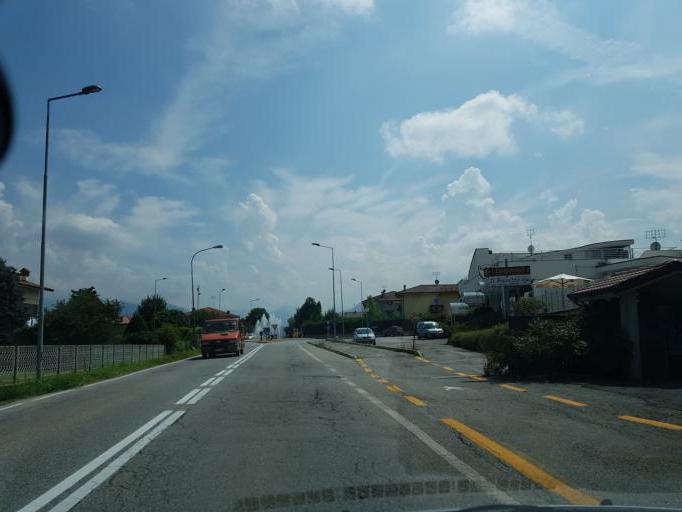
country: IT
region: Piedmont
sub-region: Provincia di Cuneo
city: Vignolo
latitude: 44.3618
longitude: 7.4757
